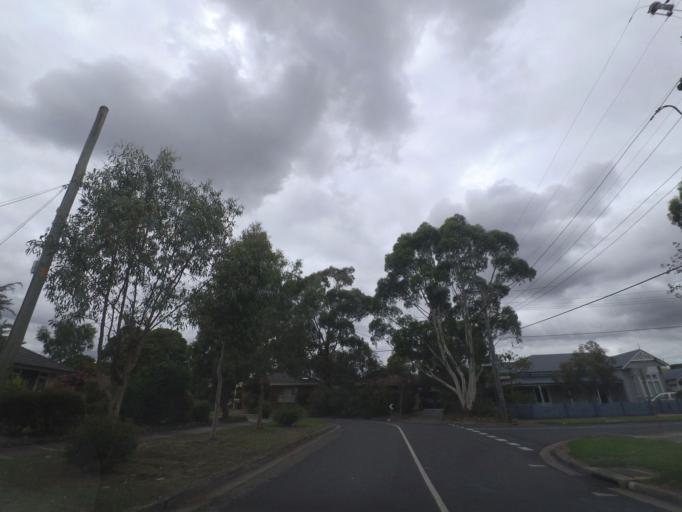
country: AU
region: Victoria
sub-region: Whitehorse
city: Forest Hill
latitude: -37.8307
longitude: 145.1677
